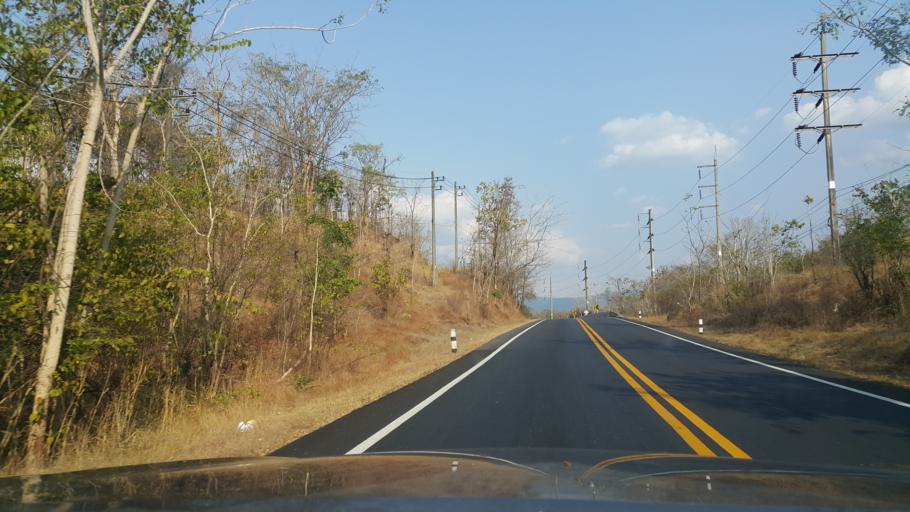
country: TH
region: Phitsanulok
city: Nakhon Thai
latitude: 17.1696
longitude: 100.9886
